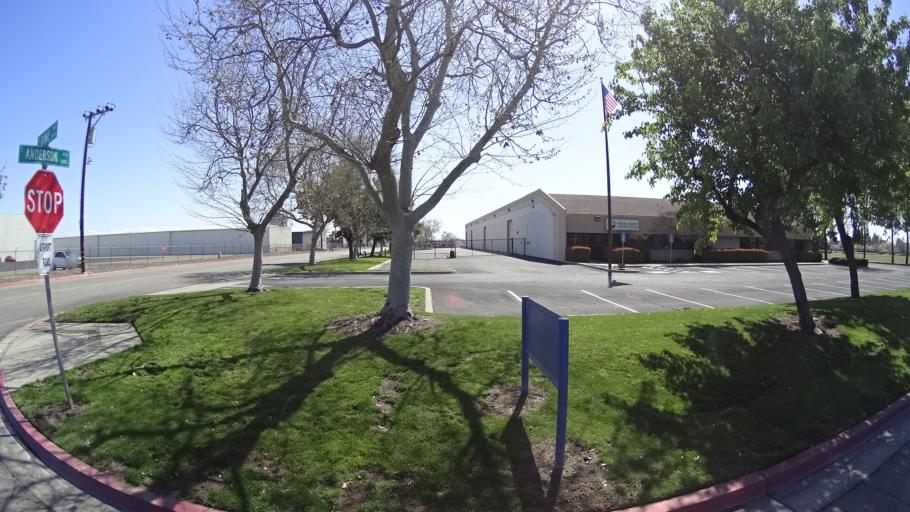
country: US
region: California
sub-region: Fresno County
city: Tarpey Village
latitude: 36.7743
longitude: -119.7260
